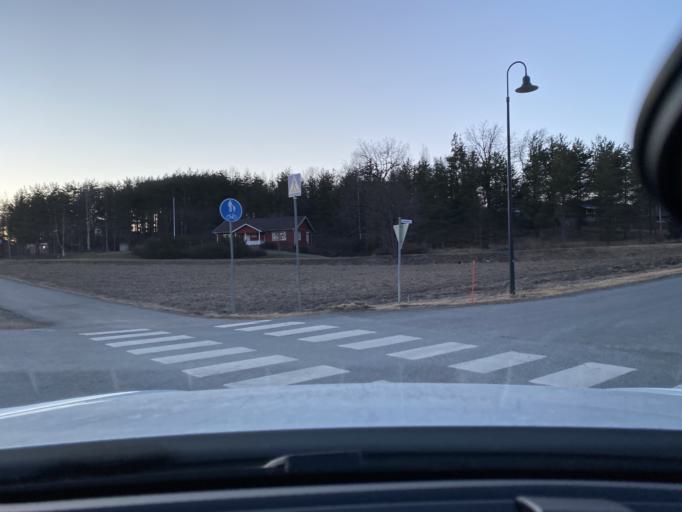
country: FI
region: Pirkanmaa
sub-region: Lounais-Pirkanmaa
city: Punkalaidun
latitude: 61.1180
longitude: 23.0796
